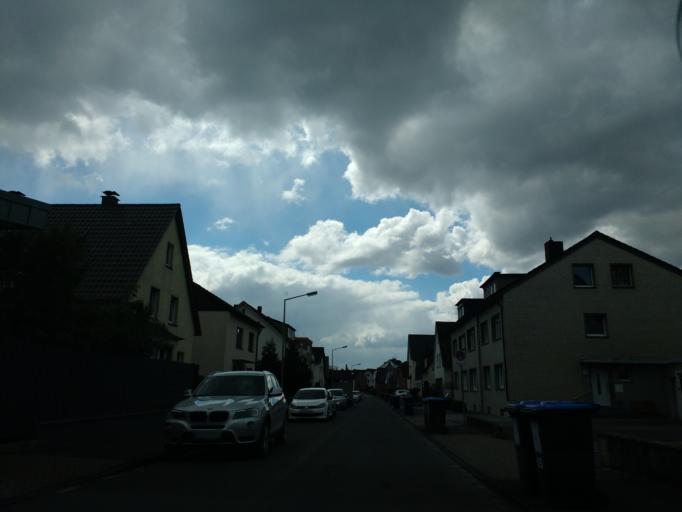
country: DE
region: North Rhine-Westphalia
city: Bad Lippspringe
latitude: 51.7909
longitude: 8.8246
